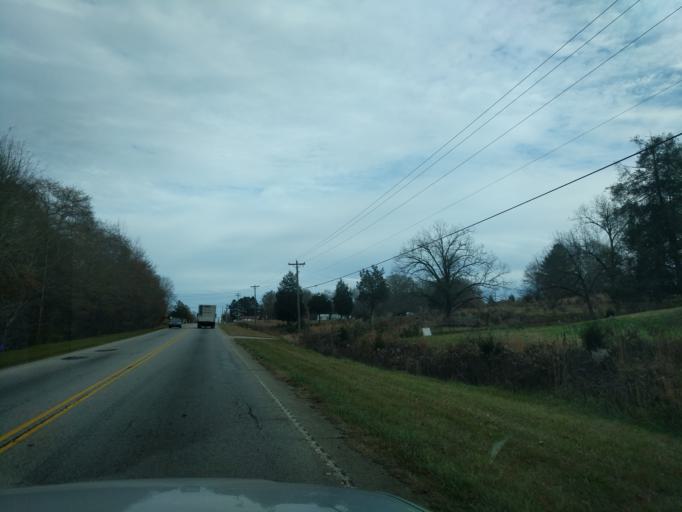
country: US
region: South Carolina
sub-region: Anderson County
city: Williamston
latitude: 34.6410
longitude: -82.4433
